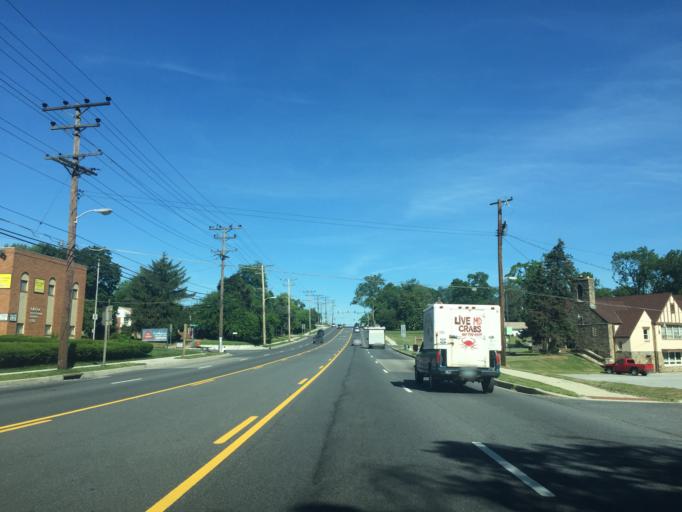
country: US
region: Maryland
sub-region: Baltimore County
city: Lochearn
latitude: 39.3464
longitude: -76.7375
